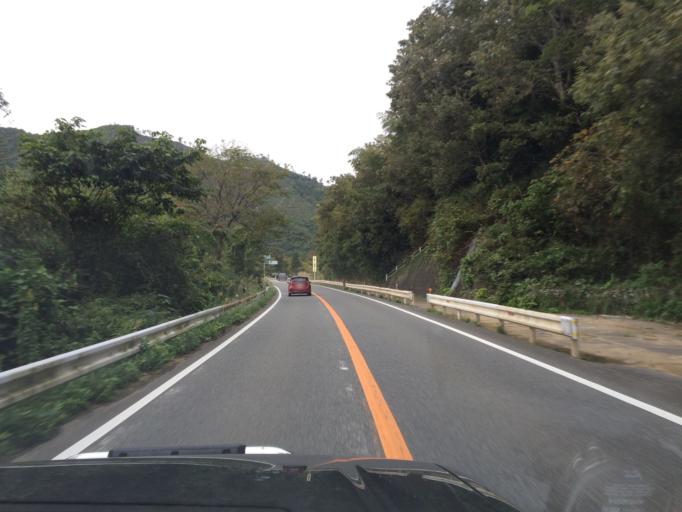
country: JP
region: Hyogo
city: Toyooka
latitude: 35.3719
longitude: 134.8165
